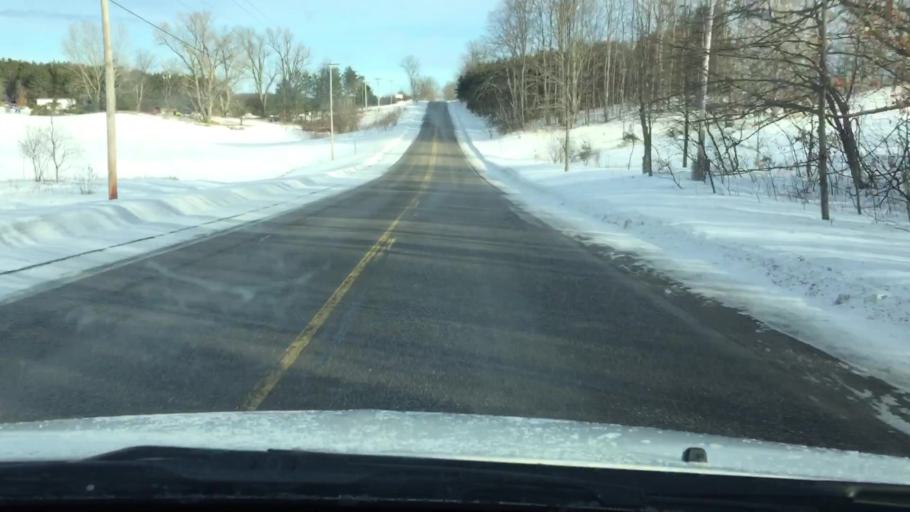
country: US
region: Michigan
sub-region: Kalkaska County
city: Kalkaska
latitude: 44.6408
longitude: -85.2263
